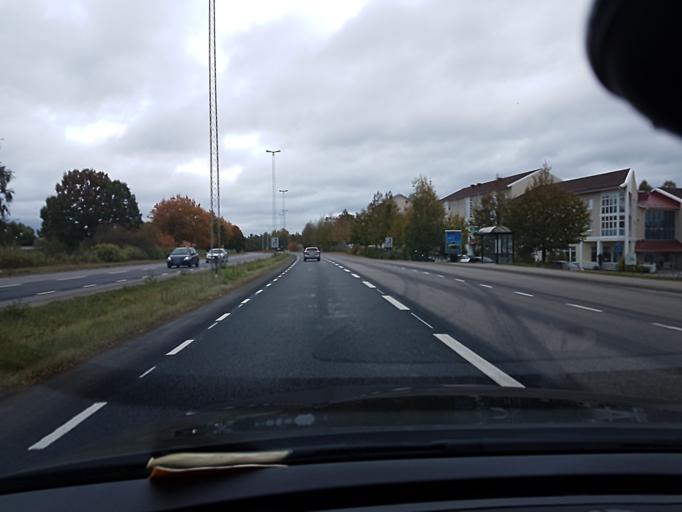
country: SE
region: Kronoberg
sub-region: Vaxjo Kommun
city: Vaexjoe
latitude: 56.8683
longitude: 14.8186
